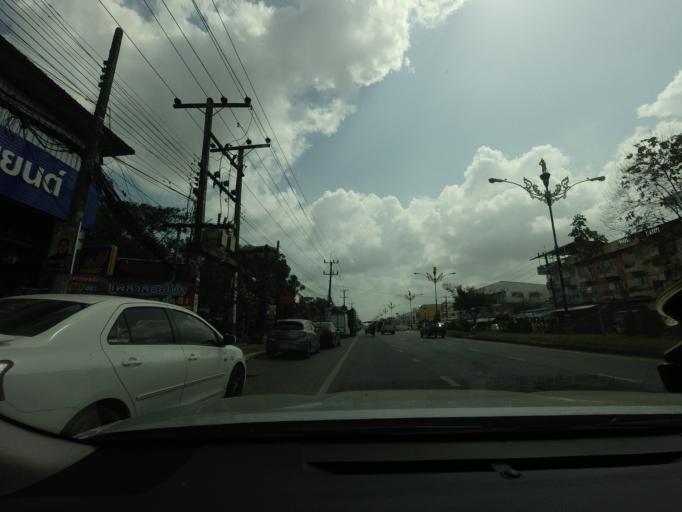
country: TH
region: Nakhon Si Thammarat
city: Nakhon Si Thammarat
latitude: 8.4342
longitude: 99.9330
